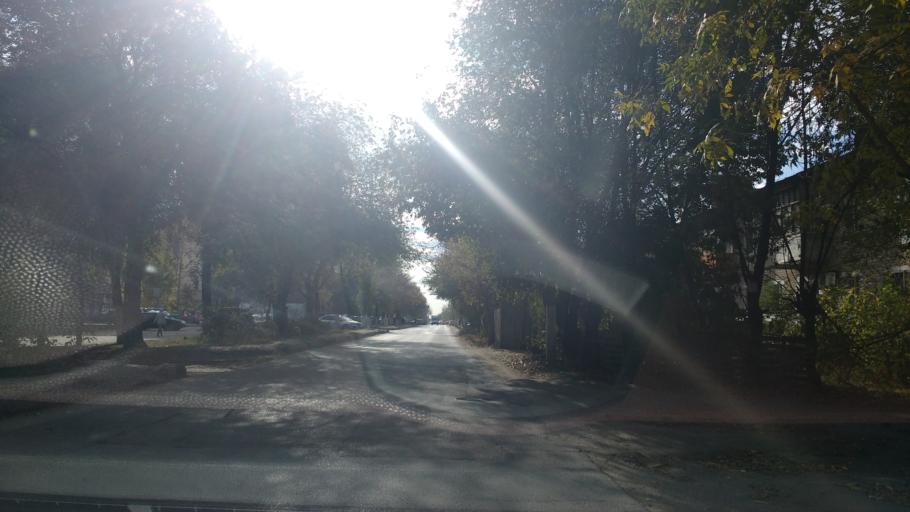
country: RU
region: Volgograd
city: Vodstroy
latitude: 48.7862
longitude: 44.5780
